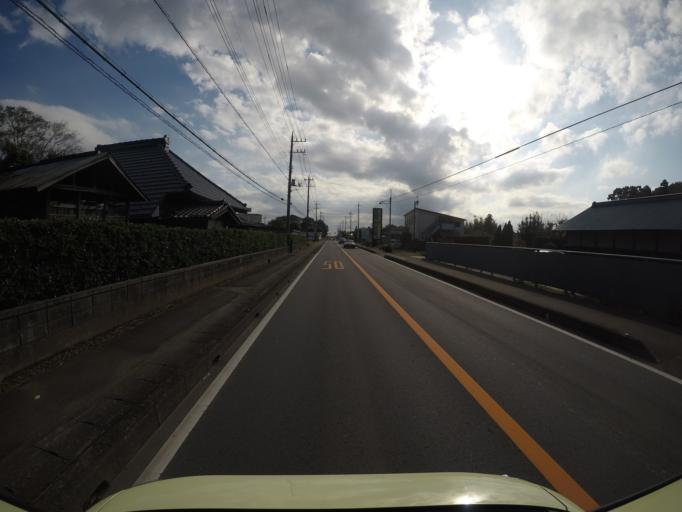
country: JP
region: Ibaraki
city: Iwai
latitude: 35.9986
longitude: 139.9040
